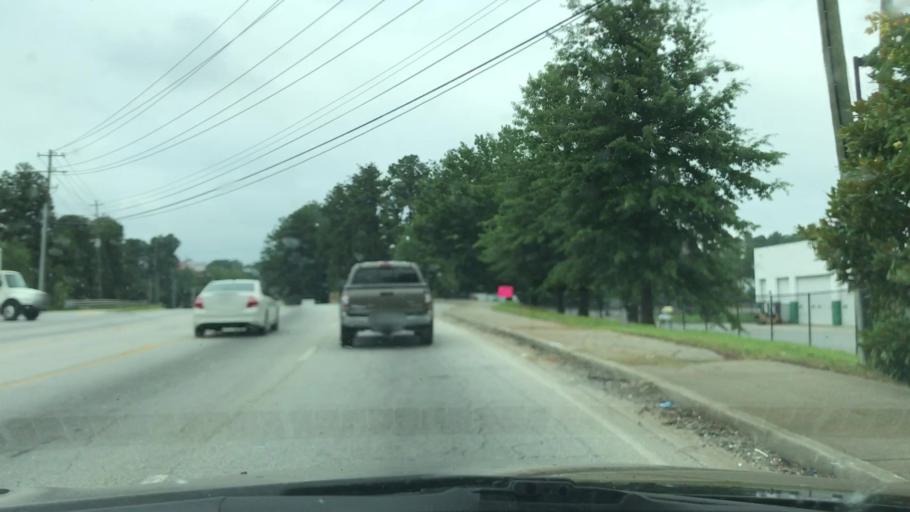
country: US
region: Georgia
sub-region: DeKalb County
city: Doraville
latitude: 33.9029
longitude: -84.2448
